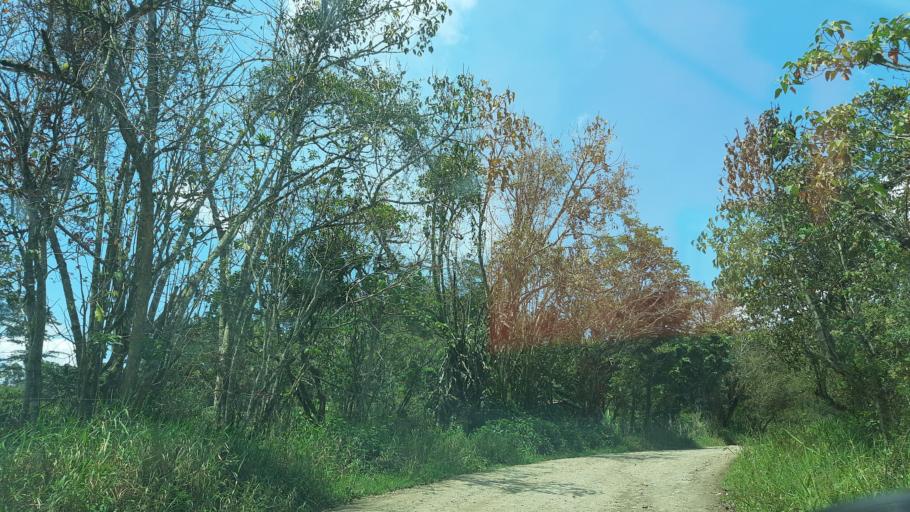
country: CO
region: Boyaca
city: Chinavita
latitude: 5.1305
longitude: -73.3682
